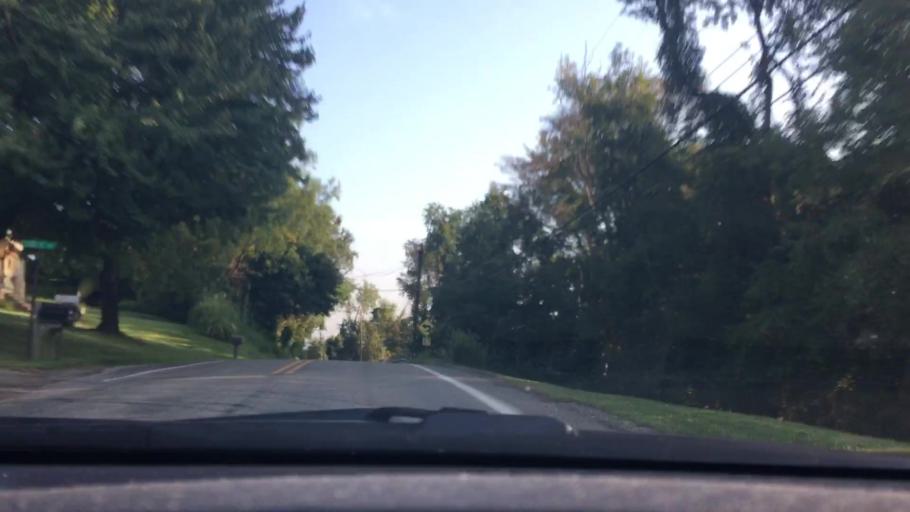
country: US
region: Pennsylvania
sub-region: Allegheny County
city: Lincoln
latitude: 40.3067
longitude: -79.8540
